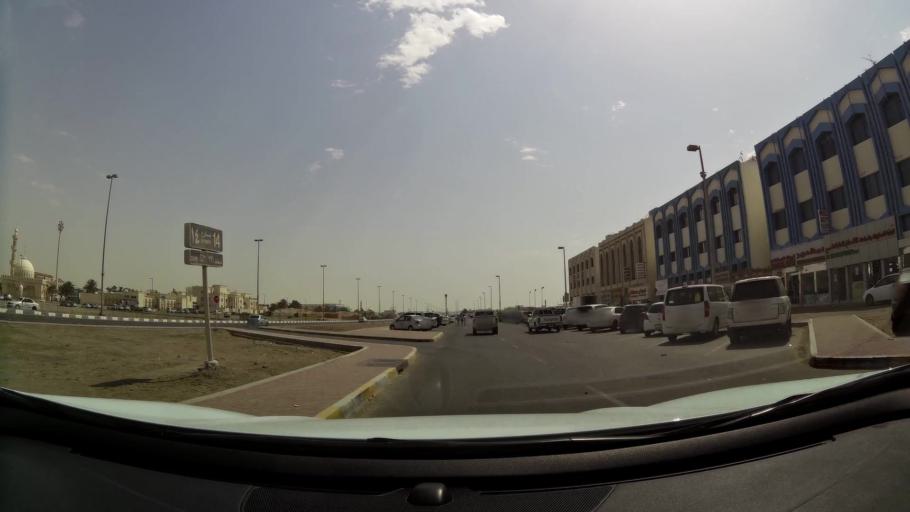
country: AE
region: Abu Dhabi
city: Abu Dhabi
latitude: 24.2964
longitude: 54.6397
